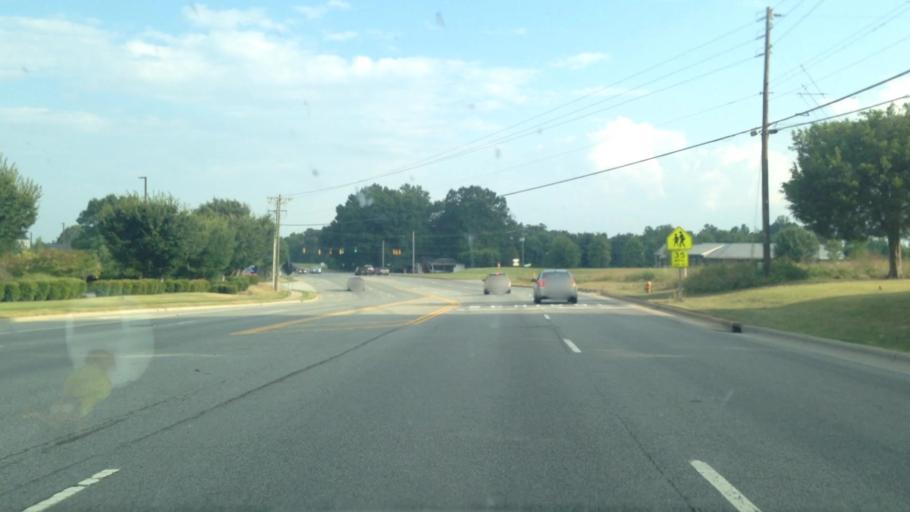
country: US
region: North Carolina
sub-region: Forsyth County
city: Kernersville
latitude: 36.0814
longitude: -80.0639
